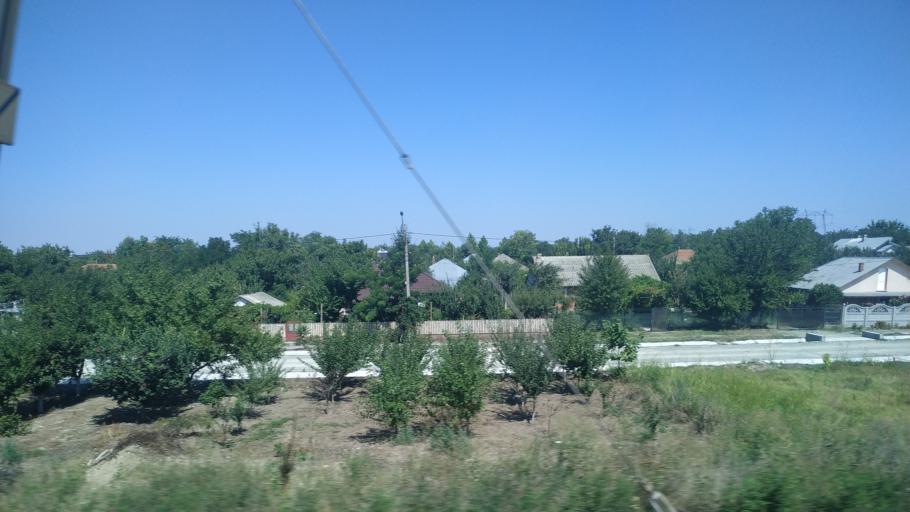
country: RO
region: Calarasi
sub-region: Comuna Perisoru
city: Perisoru
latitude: 44.4212
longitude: 27.6503
